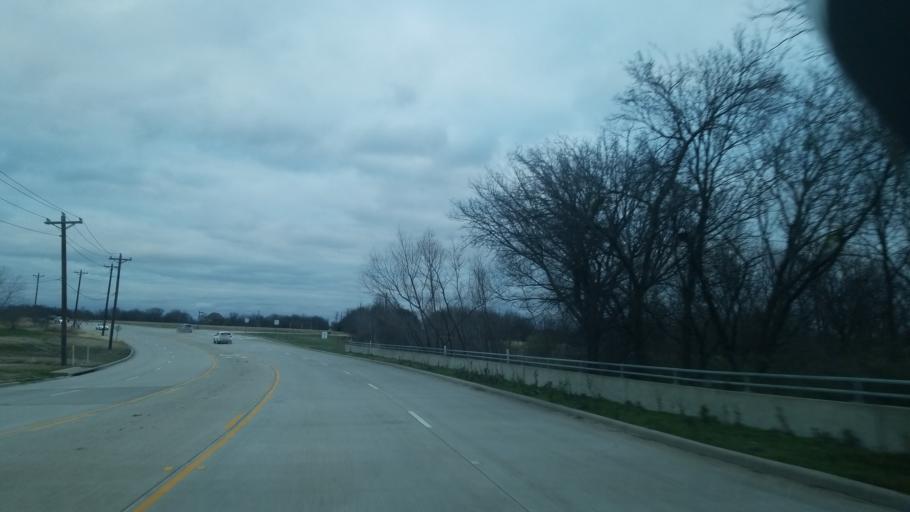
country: US
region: Texas
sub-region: Denton County
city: Little Elm
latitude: 33.1439
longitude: -96.9776
